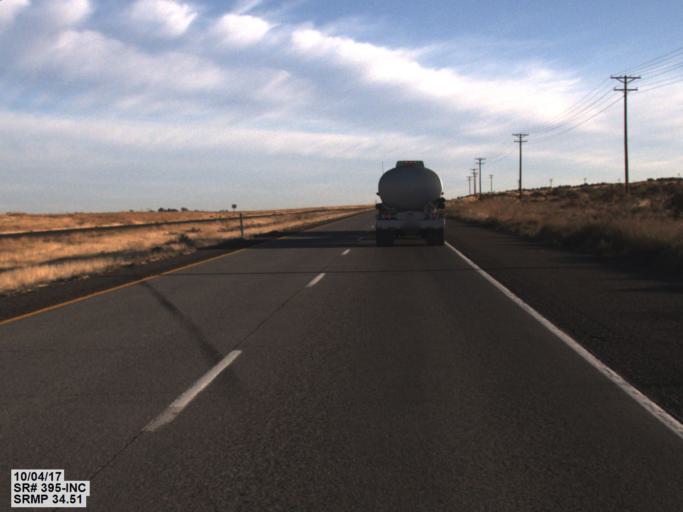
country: US
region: Washington
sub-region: Franklin County
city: Pasco
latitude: 46.4140
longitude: -119.0462
